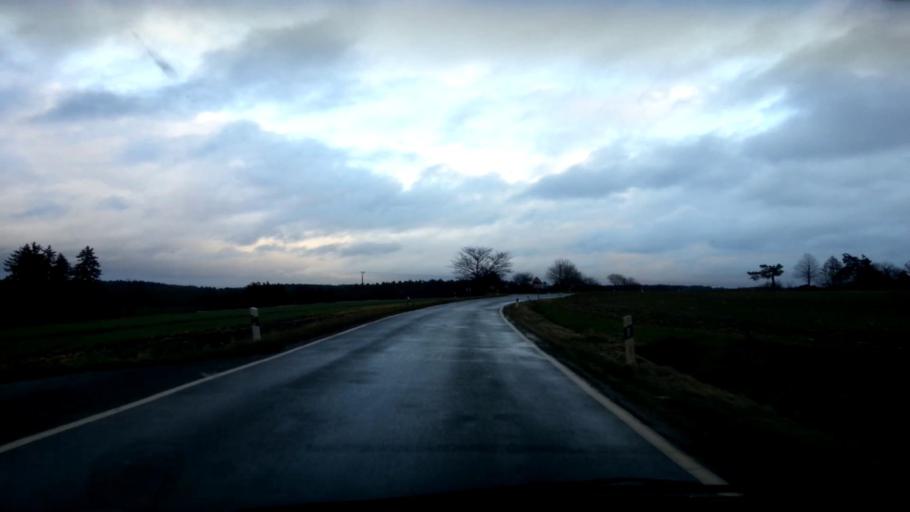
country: DE
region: Bavaria
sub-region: Upper Franconia
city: Poxdorf
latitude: 49.9232
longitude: 11.1166
